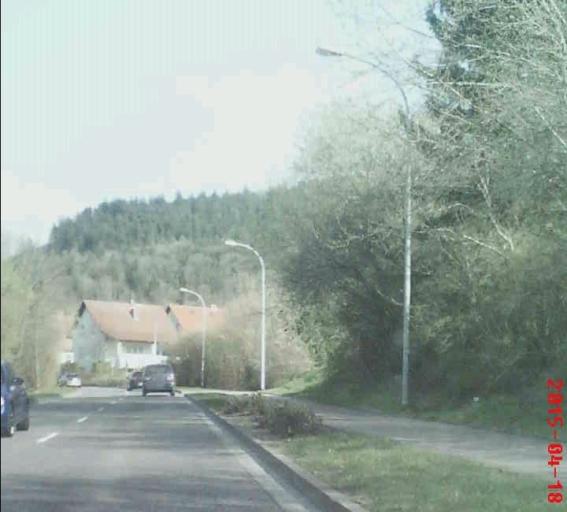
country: DE
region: Thuringia
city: Heilbad Heiligenstadt
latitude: 51.3819
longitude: 10.1537
